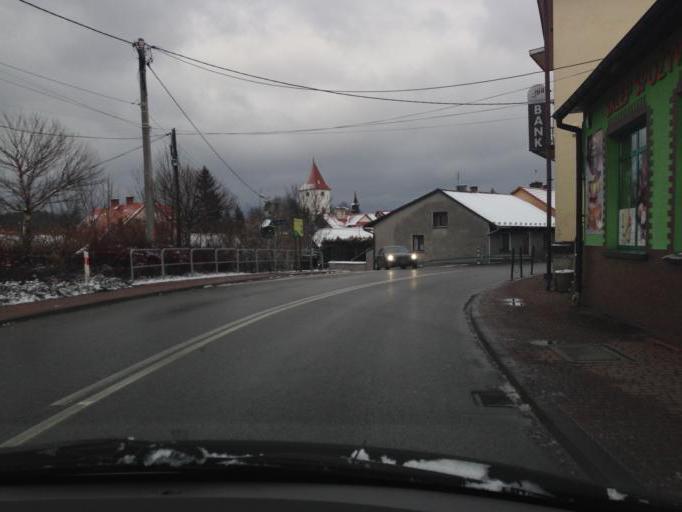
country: PL
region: Lesser Poland Voivodeship
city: Stary Wisnicz
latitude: 49.8587
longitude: 20.5250
